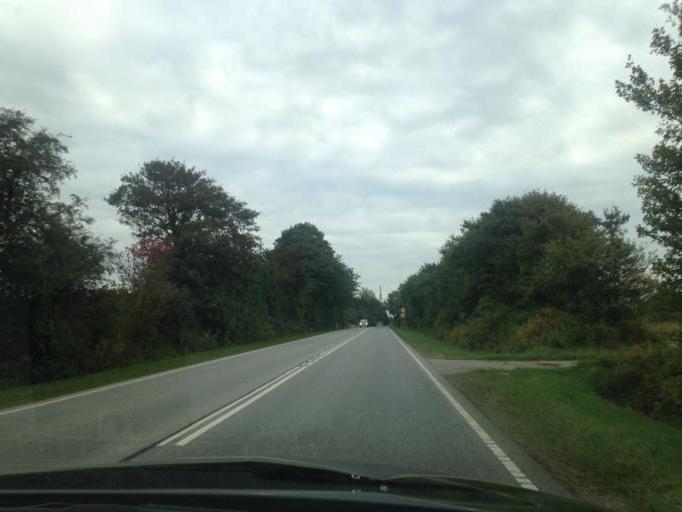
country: DK
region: South Denmark
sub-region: Haderslev Kommune
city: Vojens
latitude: 55.2554
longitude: 9.3391
